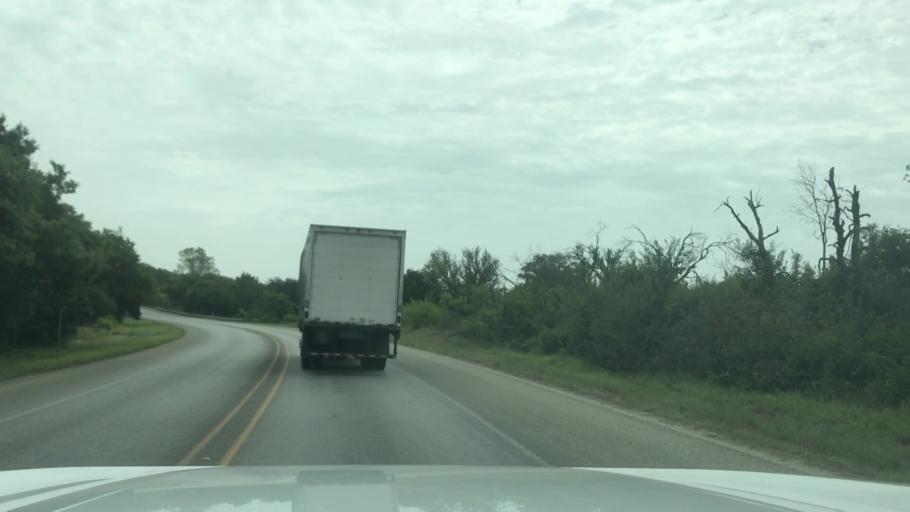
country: US
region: Texas
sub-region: Erath County
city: Dublin
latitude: 32.0877
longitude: -98.4339
